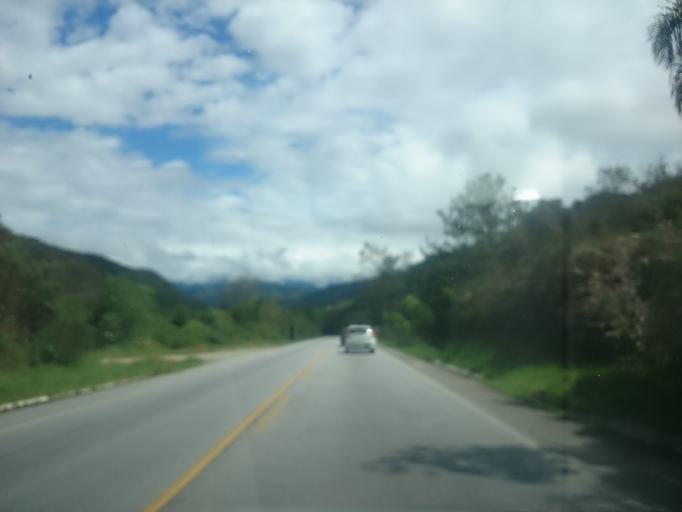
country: BR
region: Santa Catarina
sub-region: Anitapolis
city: Anitapolis
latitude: -27.6731
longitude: -49.2106
